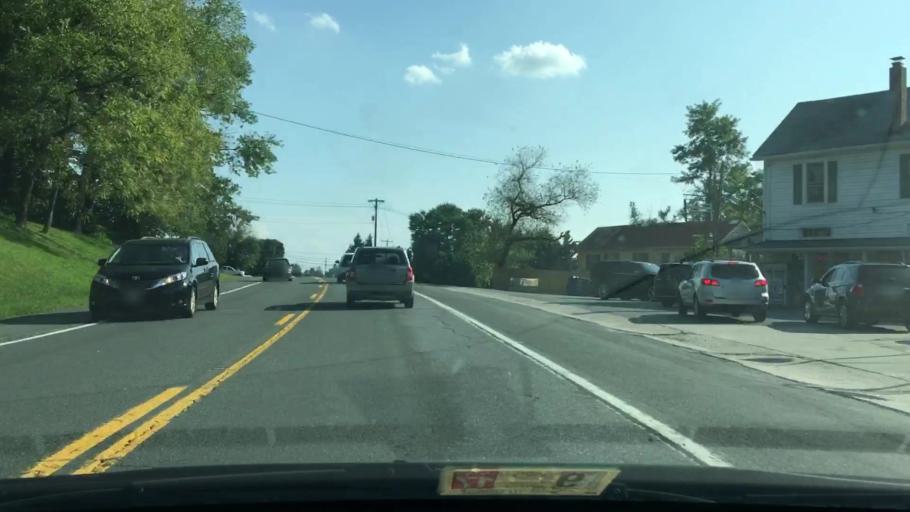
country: US
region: Maryland
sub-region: Montgomery County
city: Clarksburg
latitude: 39.2418
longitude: -77.2350
